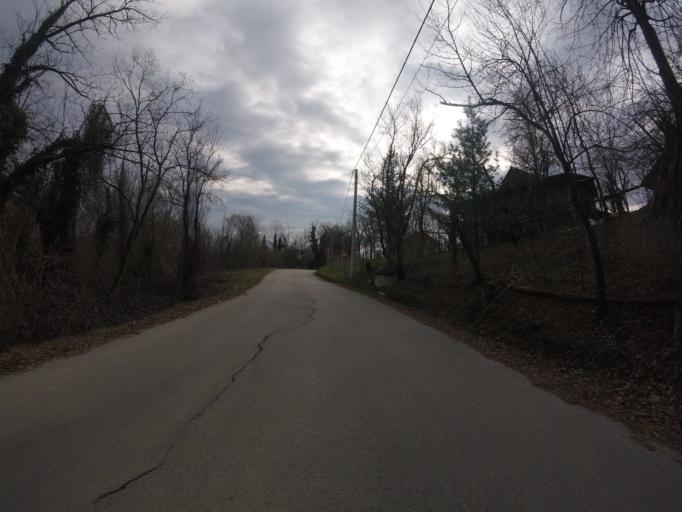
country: HR
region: Zagrebacka
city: Mraclin
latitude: 45.5142
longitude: 16.0553
